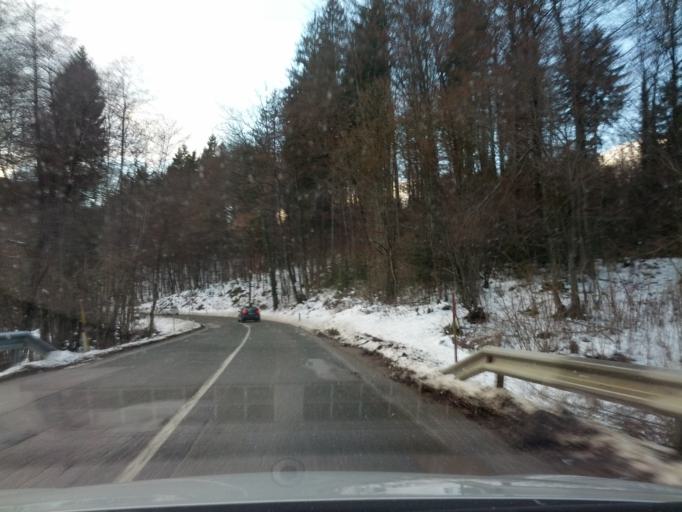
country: SI
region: Moravce
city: Moravce
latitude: 46.1373
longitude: 14.8112
